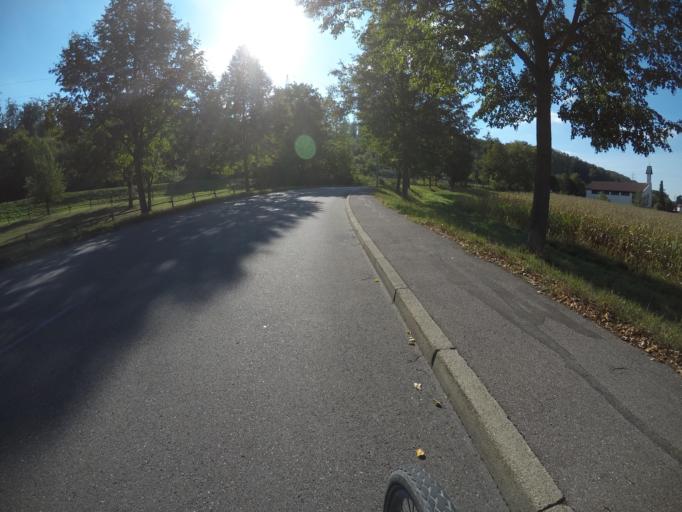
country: DE
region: Baden-Wuerttemberg
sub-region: Regierungsbezirk Stuttgart
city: Denkendorf
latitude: 48.7187
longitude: 9.3360
